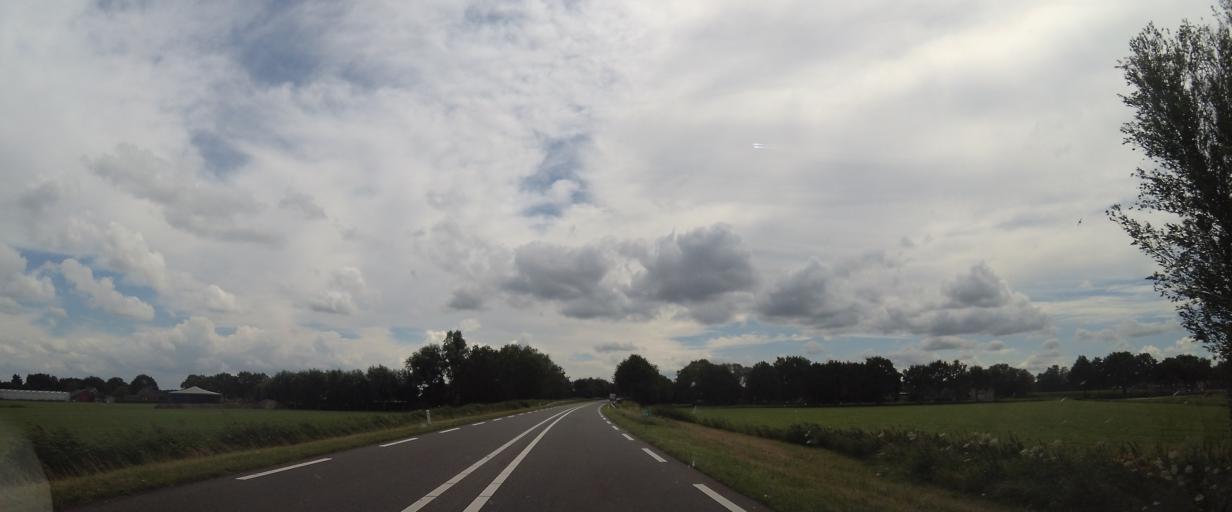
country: NL
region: North Brabant
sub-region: Gemeente Breda
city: Hoge Vucht
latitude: 51.6417
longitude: 4.7676
